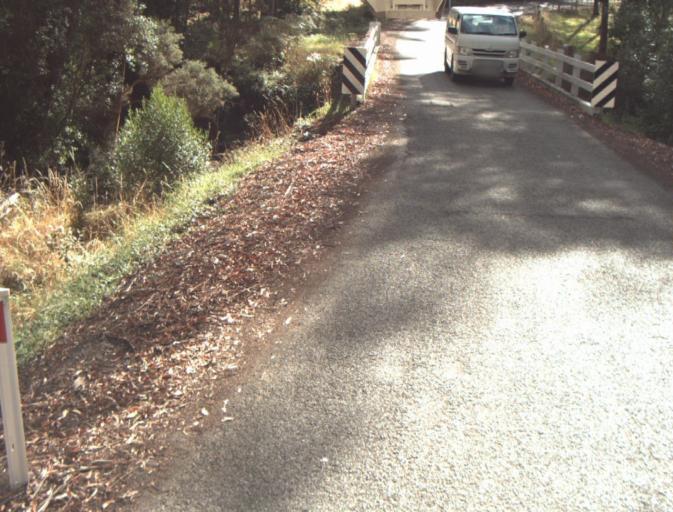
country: AU
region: Tasmania
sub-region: Launceston
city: Mayfield
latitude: -41.2697
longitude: 147.1633
